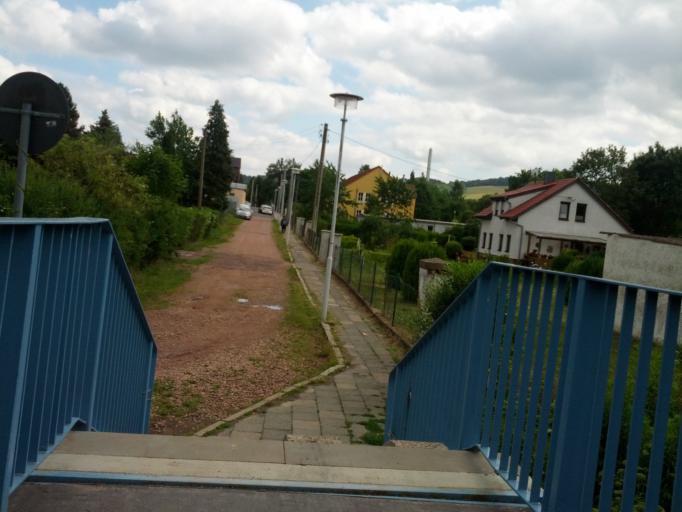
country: DE
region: Thuringia
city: Eisenach
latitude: 50.9803
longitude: 10.3416
